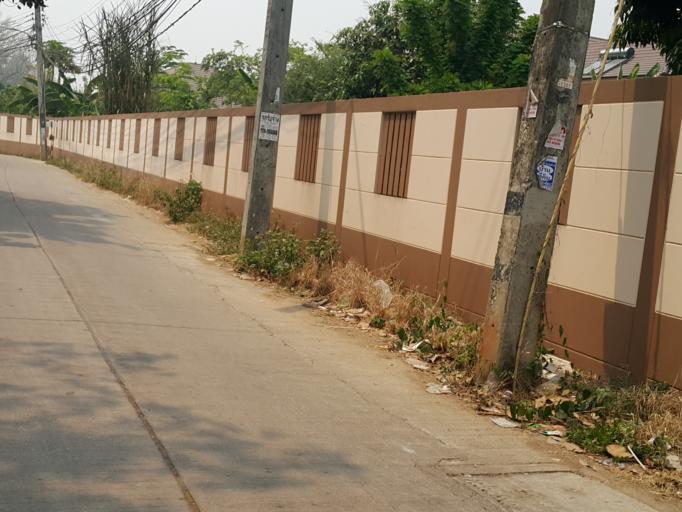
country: TH
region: Chiang Mai
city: Saraphi
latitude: 18.7393
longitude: 99.0238
